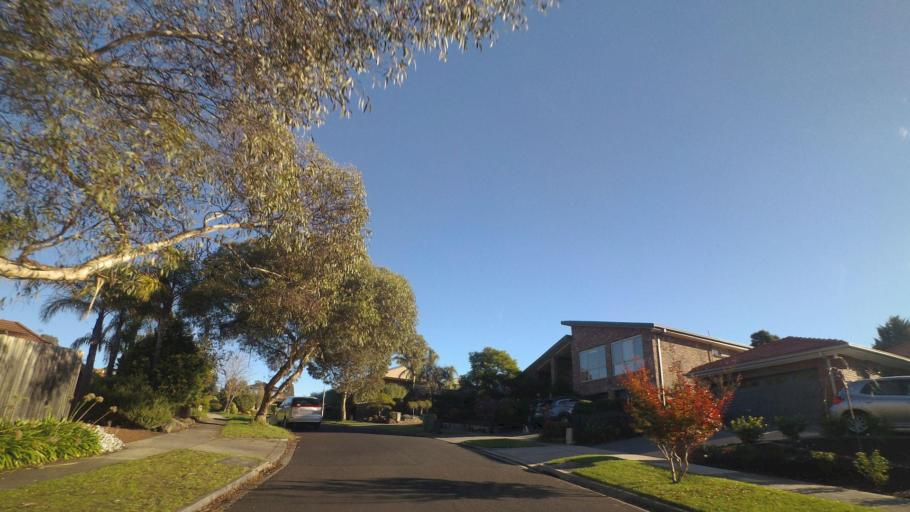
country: AU
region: Victoria
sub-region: Banyule
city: Yallambie
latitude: -37.7321
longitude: 145.0990
